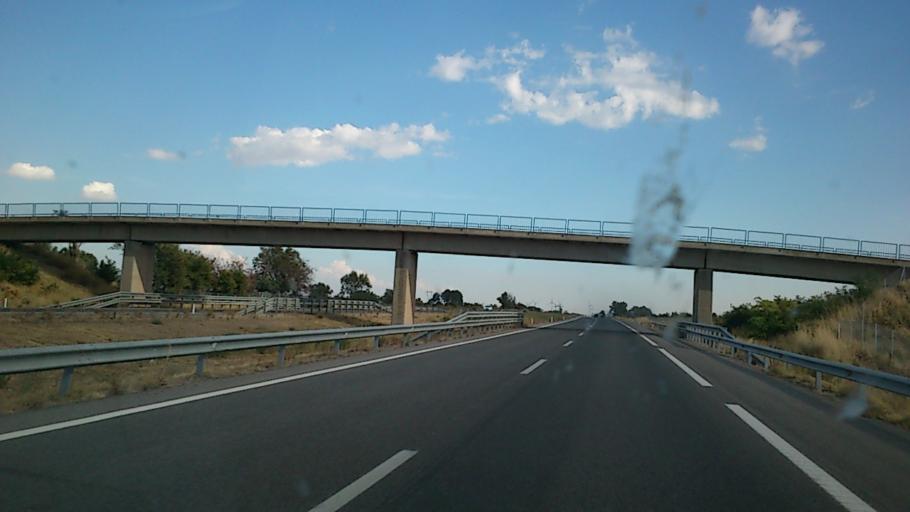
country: ES
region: Aragon
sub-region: Provincia de Zaragoza
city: Frescano
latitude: 41.9142
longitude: -1.4702
